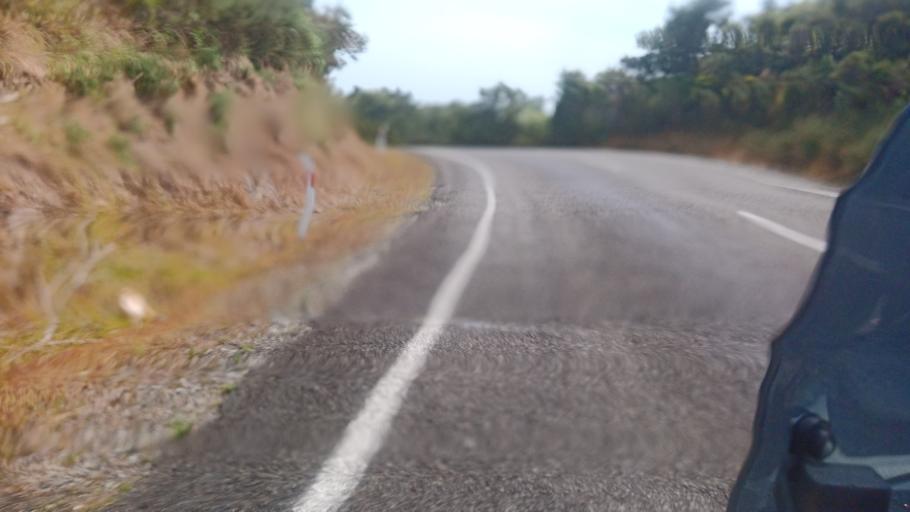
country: NZ
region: Bay of Plenty
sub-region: Opotiki District
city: Opotiki
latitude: -37.5911
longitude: 178.1660
